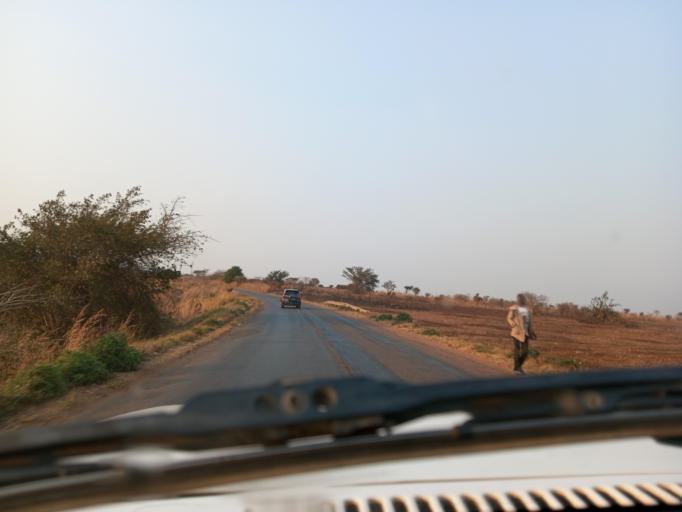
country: ZM
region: Northern
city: Mpika
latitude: -11.9011
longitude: 31.4138
